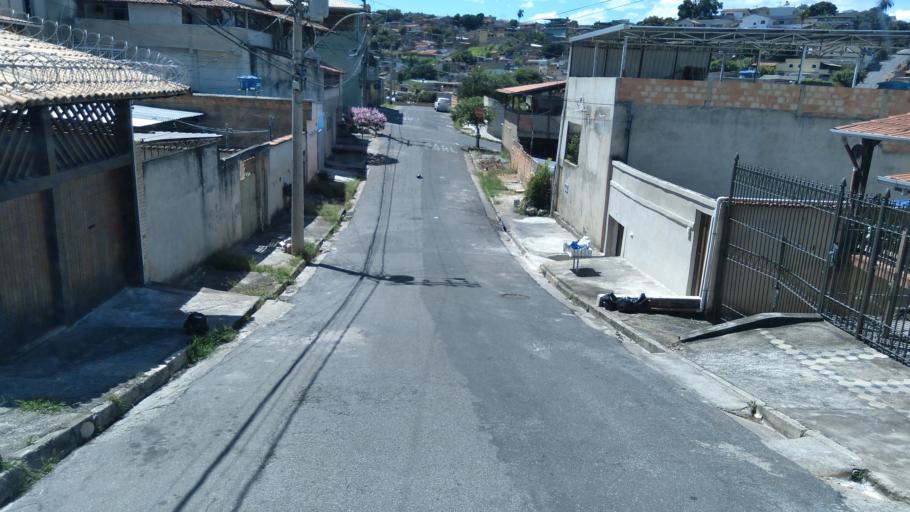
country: BR
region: Minas Gerais
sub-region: Belo Horizonte
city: Belo Horizonte
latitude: -19.8494
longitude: -43.8970
